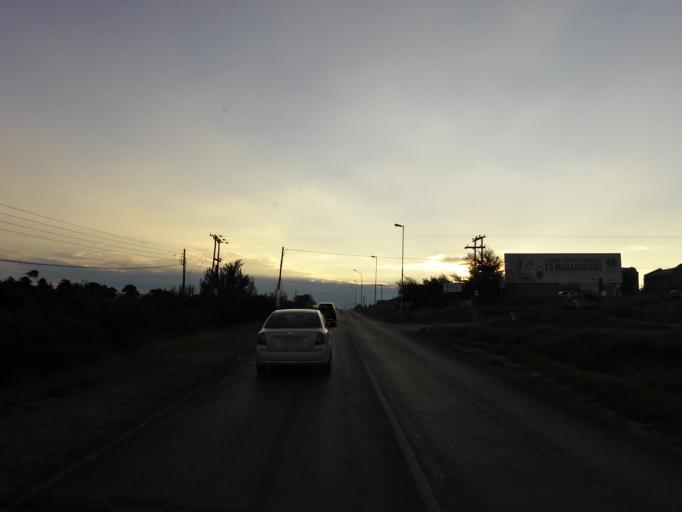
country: LS
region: Leribe
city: Leribe
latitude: -28.8685
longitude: 28.0613
